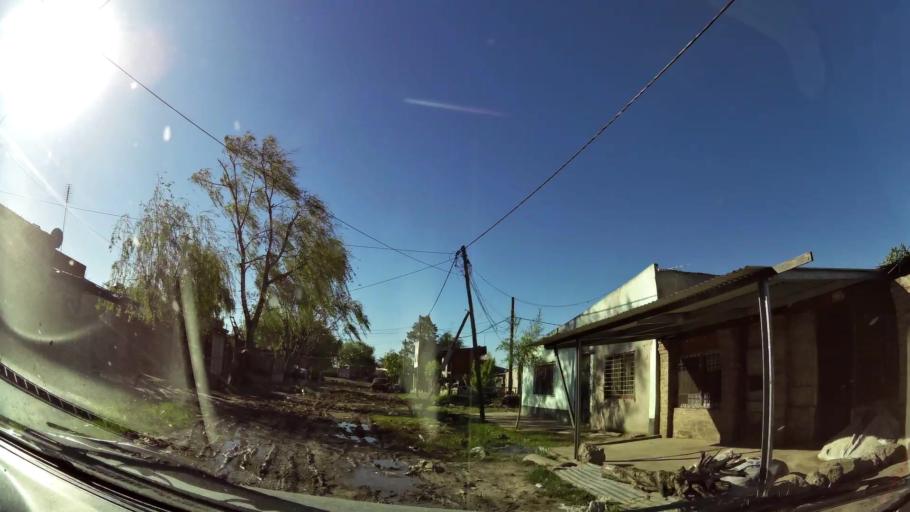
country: AR
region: Buenos Aires
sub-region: Partido de Almirante Brown
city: Adrogue
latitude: -34.7576
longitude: -58.3217
